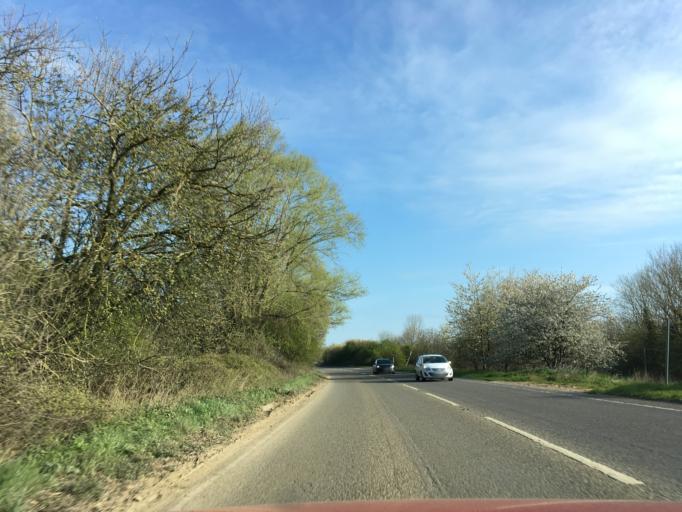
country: GB
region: England
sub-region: Milton Keynes
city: Stony Stratford
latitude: 52.0555
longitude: -0.8700
